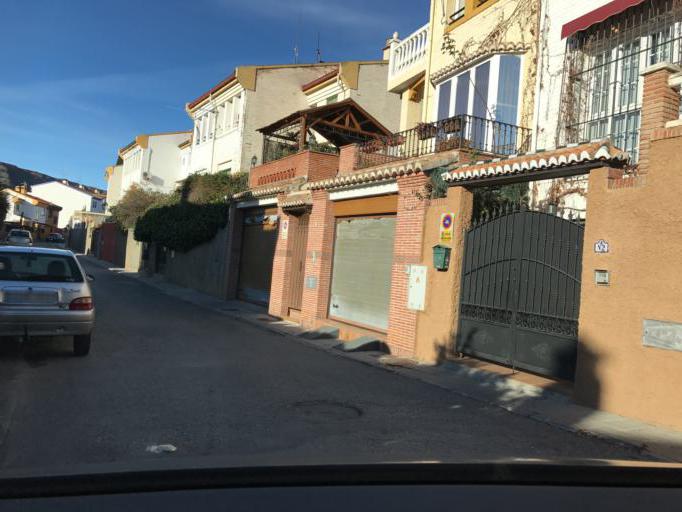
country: ES
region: Andalusia
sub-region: Provincia de Granada
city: Cenes de la Vega
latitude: 37.1619
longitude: -3.5419
